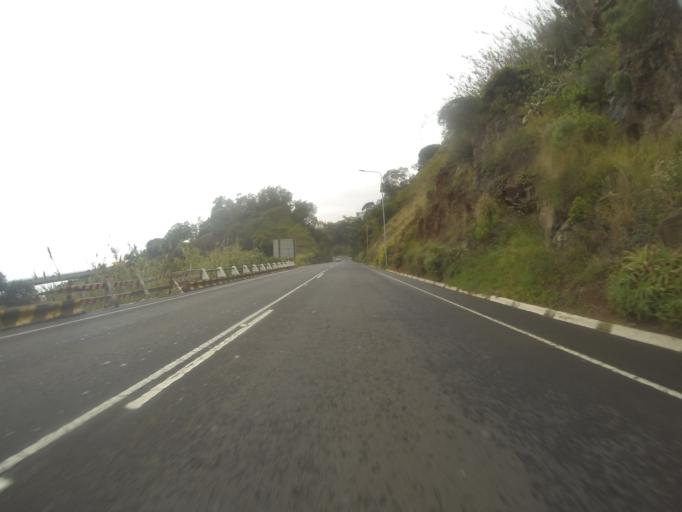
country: PT
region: Madeira
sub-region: Funchal
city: Nossa Senhora do Monte
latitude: 32.6563
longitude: -16.8789
